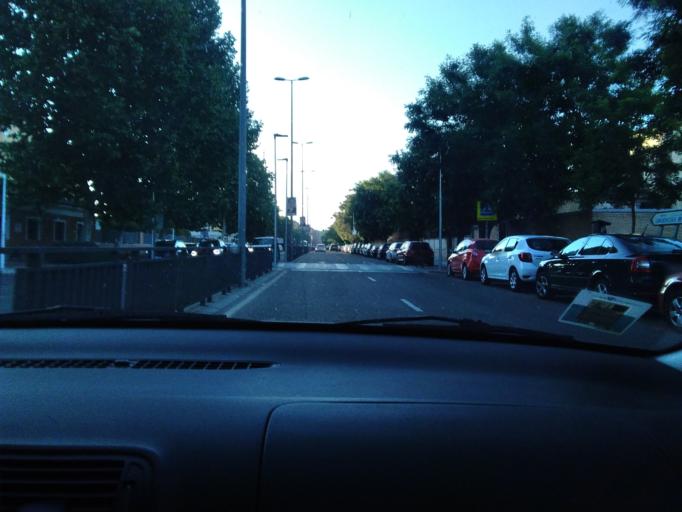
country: ES
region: Castille-La Mancha
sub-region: Province of Toledo
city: Toledo
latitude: 39.8713
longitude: -4.0366
